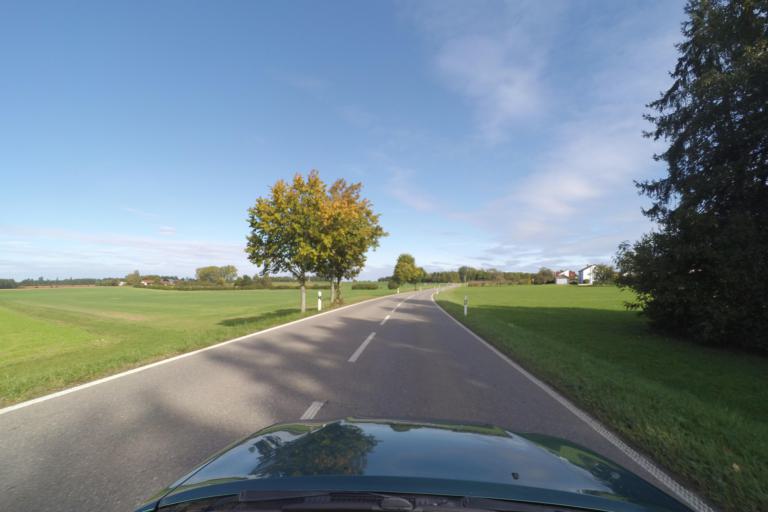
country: DE
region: Baden-Wuerttemberg
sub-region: Karlsruhe Region
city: Nagold
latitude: 48.5001
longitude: 8.7212
